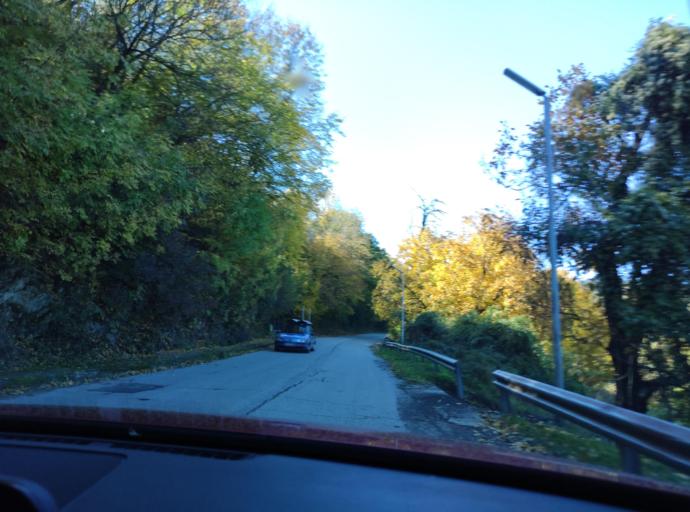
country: BG
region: Montana
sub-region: Obshtina Chiprovtsi
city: Chiprovtsi
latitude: 43.3816
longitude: 22.8964
